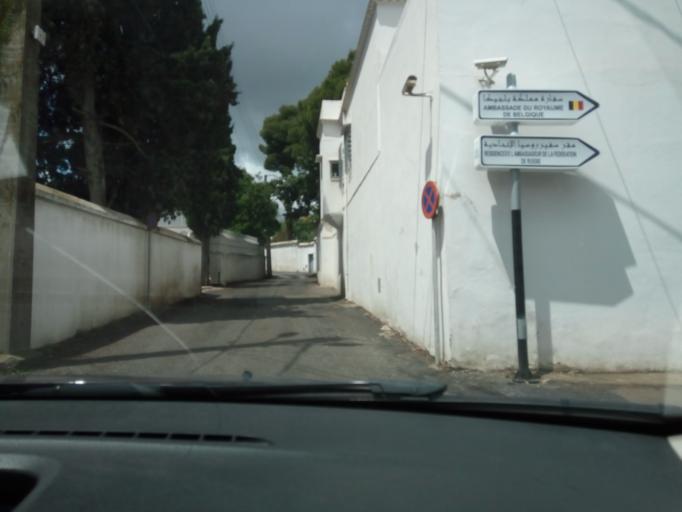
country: DZ
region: Alger
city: Algiers
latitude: 36.7649
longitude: 3.0335
